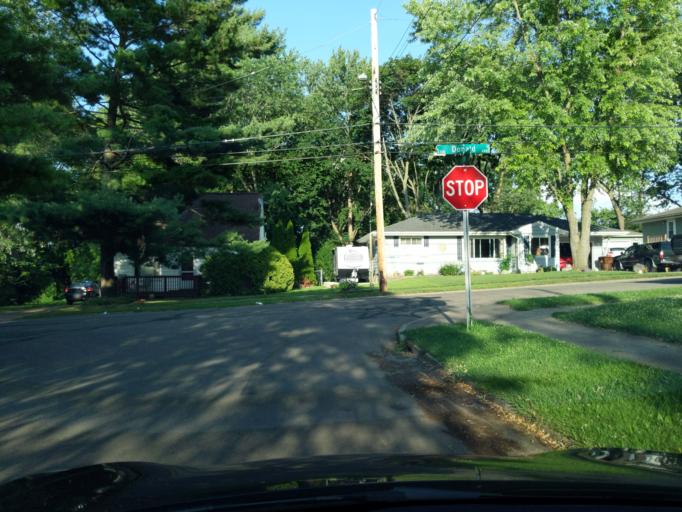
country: US
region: Michigan
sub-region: Ingham County
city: Lansing
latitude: 42.6894
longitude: -84.5507
